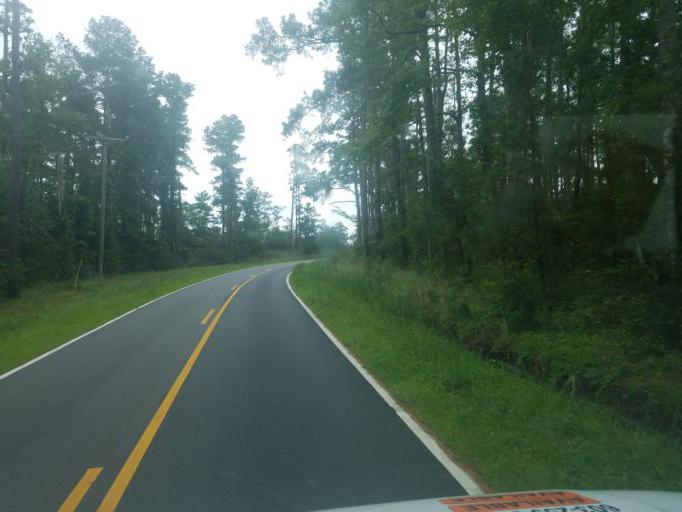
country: US
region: North Carolina
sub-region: Dare County
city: Manteo
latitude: 35.8801
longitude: -75.7593
